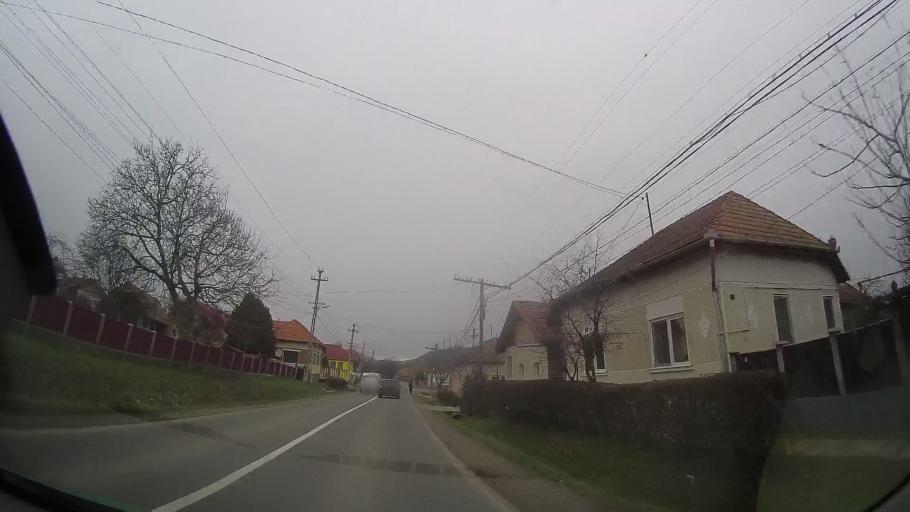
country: RO
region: Mures
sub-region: Comuna Ceausu de Campie
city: Ceausu de Campie
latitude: 46.6163
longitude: 24.5261
